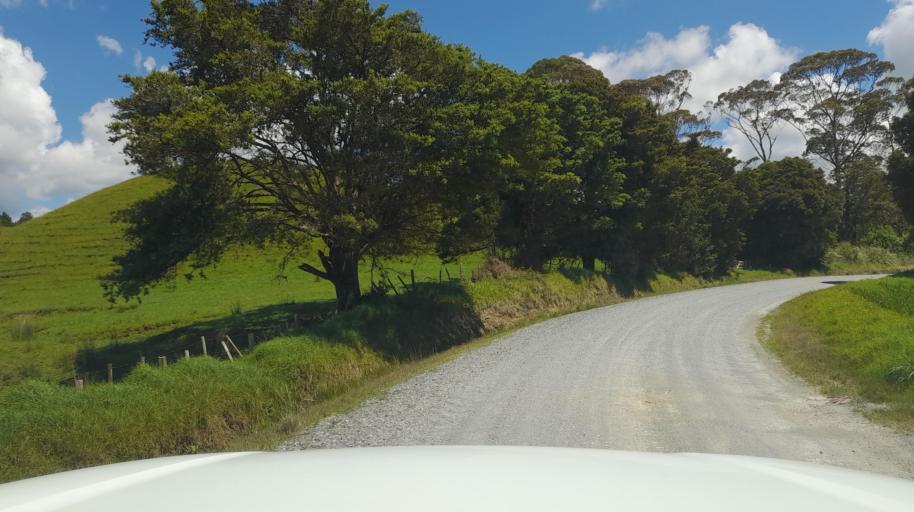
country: NZ
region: Northland
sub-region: Far North District
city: Kaitaia
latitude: -35.1131
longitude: 173.3969
